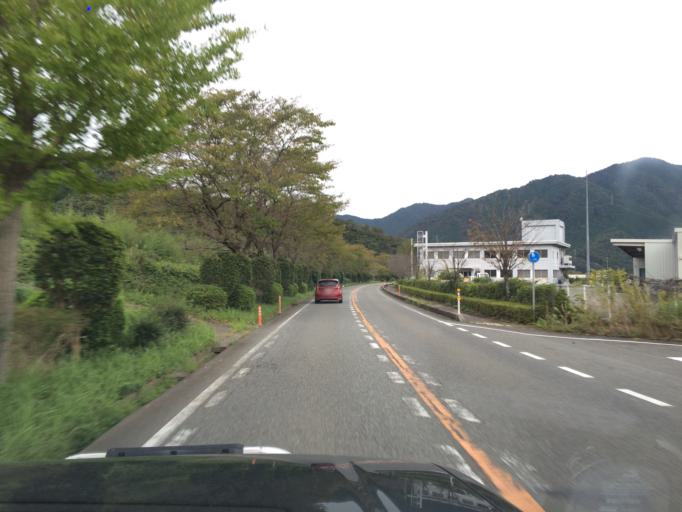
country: JP
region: Hyogo
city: Toyooka
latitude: 35.3746
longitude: 134.8139
